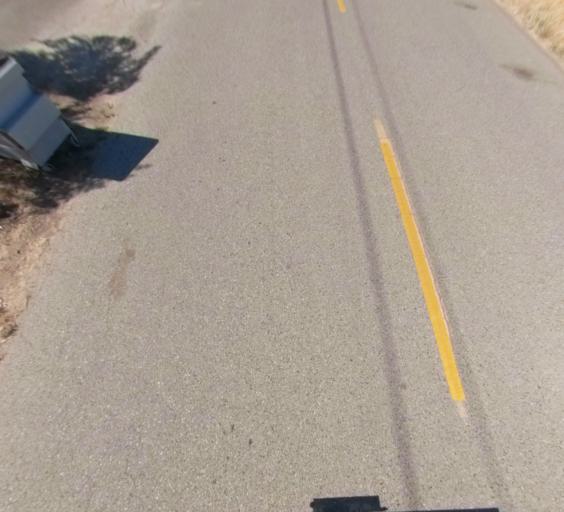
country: US
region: California
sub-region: Madera County
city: Bonadelle Ranchos-Madera Ranchos
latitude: 36.9844
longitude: -119.8721
